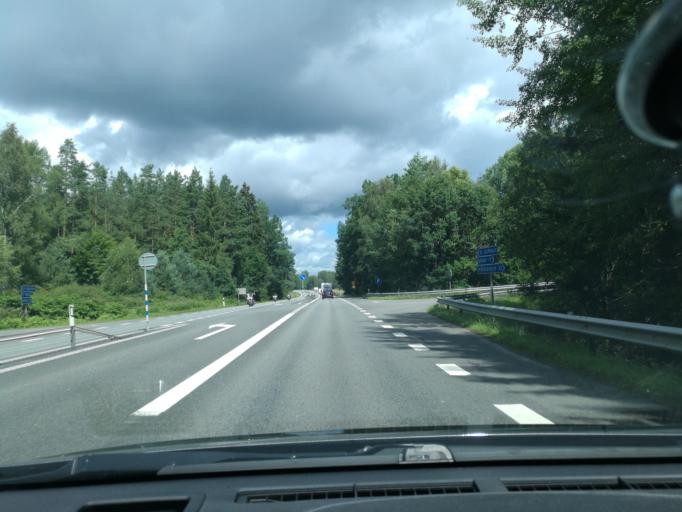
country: SE
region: Skane
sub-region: Osby Kommun
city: Osby
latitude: 56.3723
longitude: 14.0320
